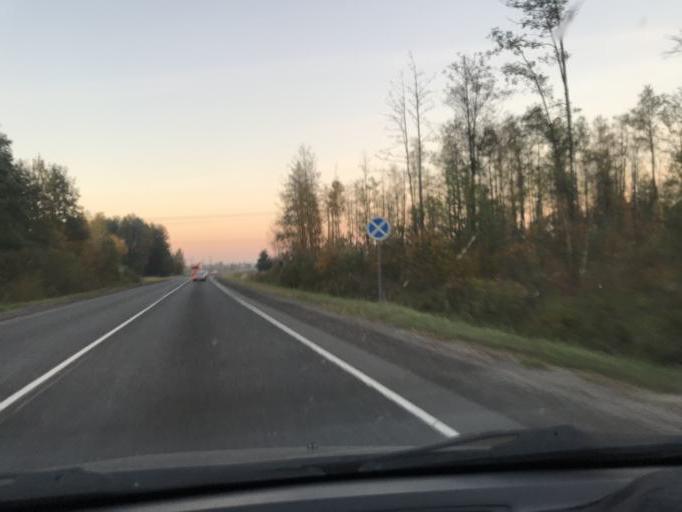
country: BY
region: Mogilev
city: Babruysk
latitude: 53.1696
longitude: 29.0446
